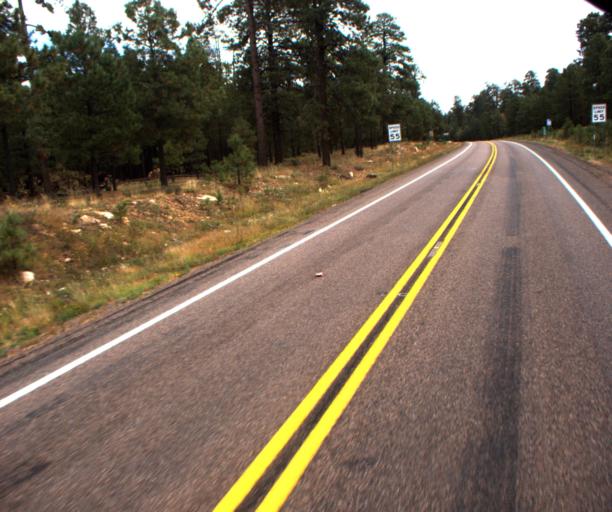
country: US
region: Arizona
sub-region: Navajo County
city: Heber-Overgaard
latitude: 34.3300
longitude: -110.7736
